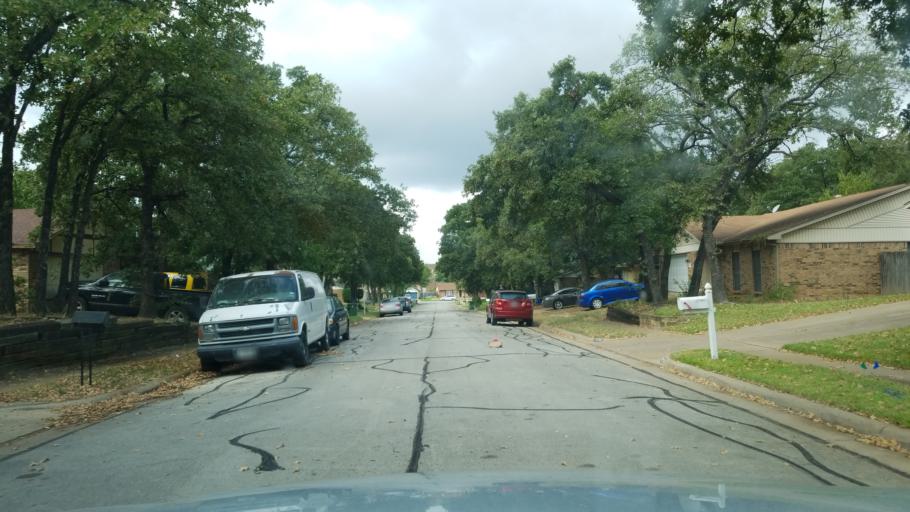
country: US
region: Texas
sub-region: Tarrant County
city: Euless
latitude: 32.8483
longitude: -97.1068
